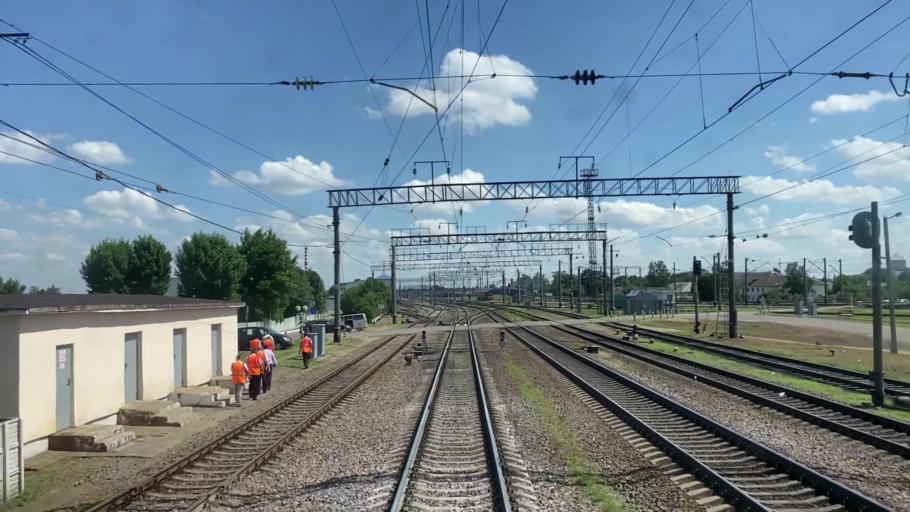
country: BY
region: Brest
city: Baranovichi
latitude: 53.1285
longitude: 25.9838
